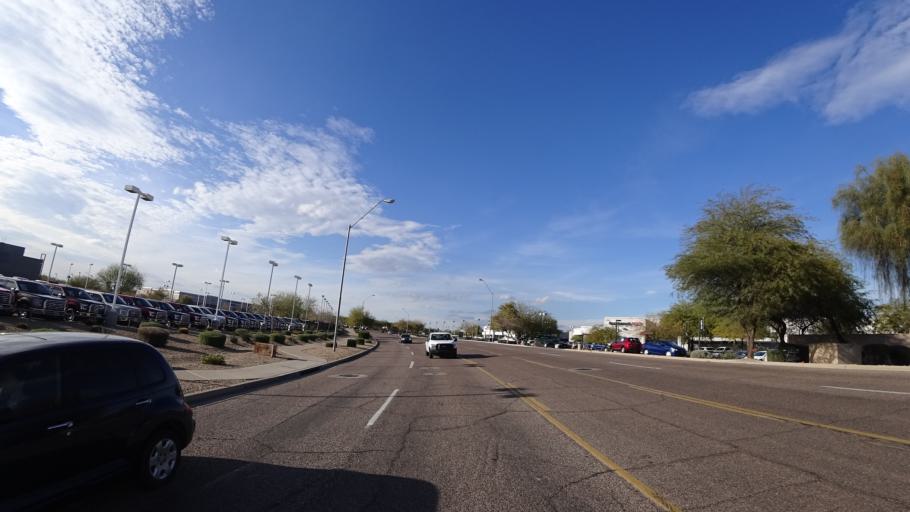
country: US
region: Arizona
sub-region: Maricopa County
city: Sun City
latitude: 33.6401
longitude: -112.2532
